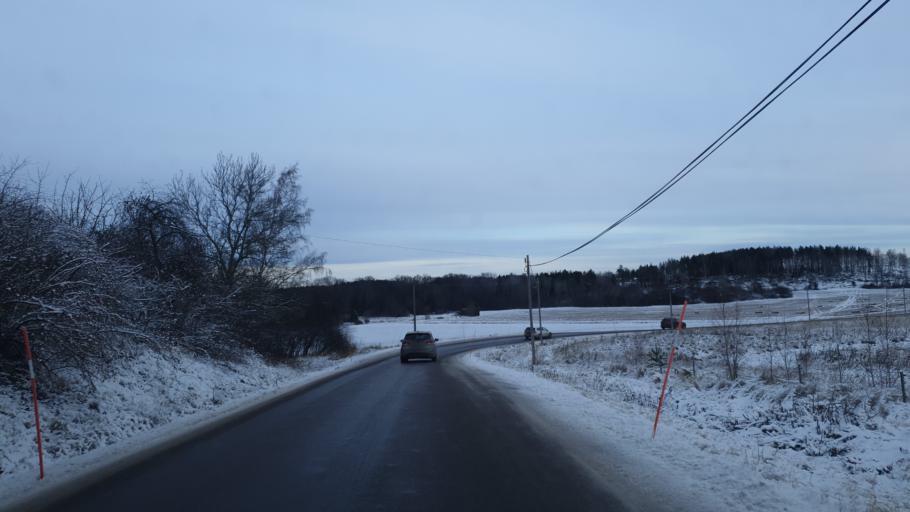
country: SE
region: Uppsala
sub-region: Habo Kommun
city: Balsta
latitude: 59.7080
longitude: 17.5613
